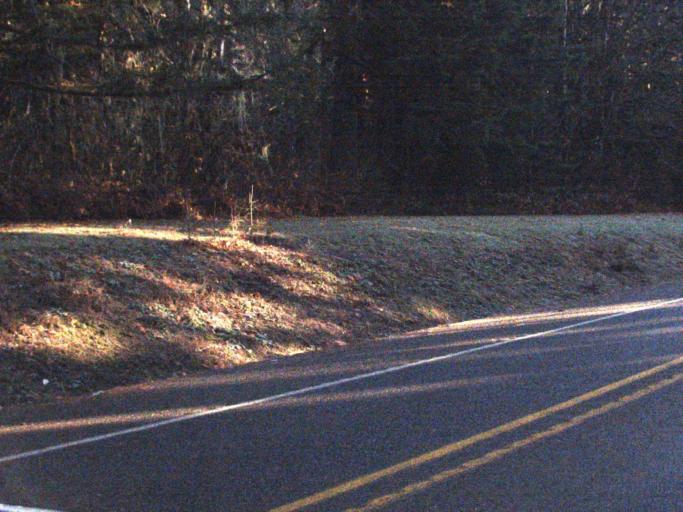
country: US
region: Washington
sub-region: Snohomish County
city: Darrington
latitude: 48.4874
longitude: -121.6138
